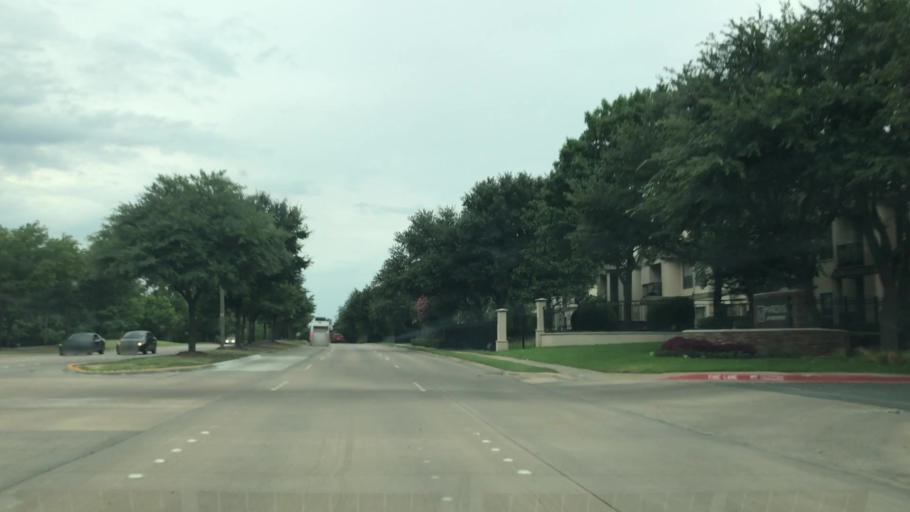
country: US
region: Texas
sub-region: Collin County
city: Plano
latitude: 32.9977
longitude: -96.7337
